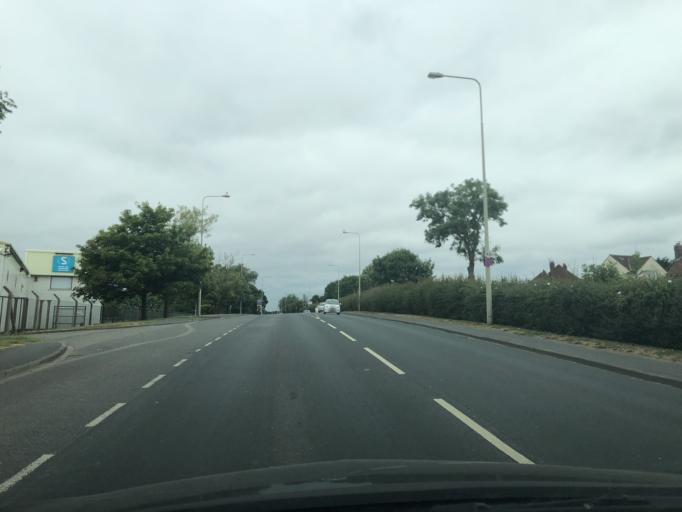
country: GB
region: England
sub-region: North Yorkshire
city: Scarborough
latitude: 54.2388
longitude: -0.4060
